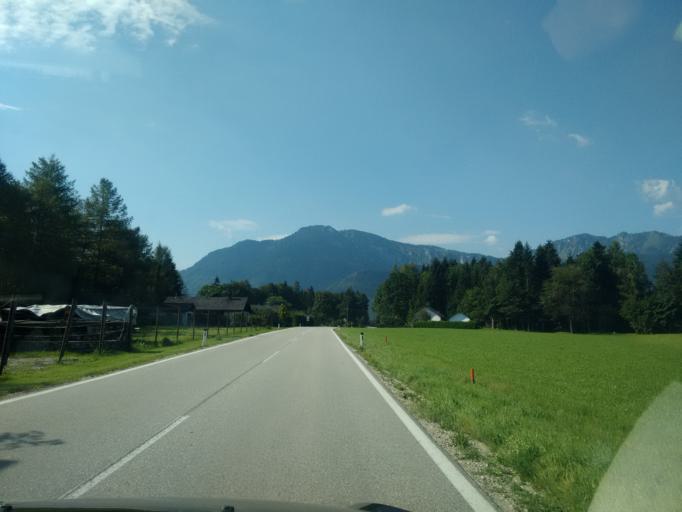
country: AT
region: Upper Austria
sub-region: Politischer Bezirk Gmunden
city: Scharnstein
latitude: 47.8936
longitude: 13.9485
